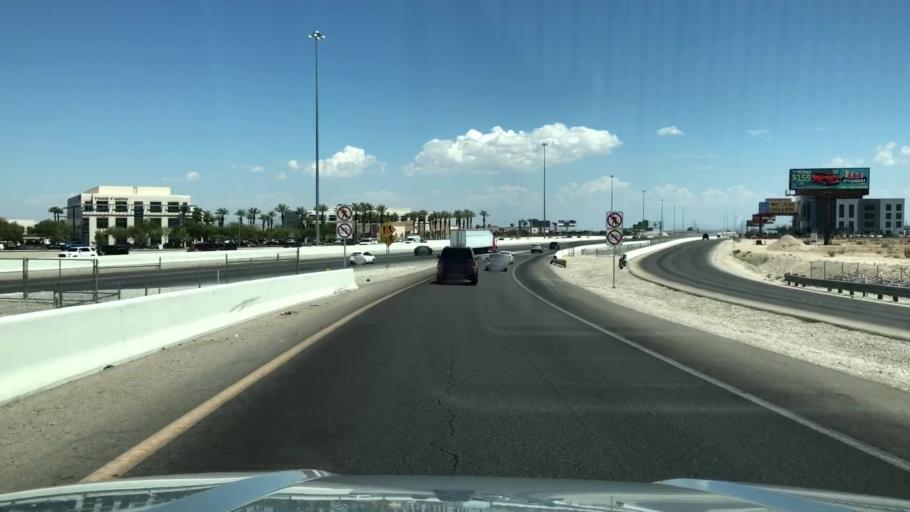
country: US
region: Nevada
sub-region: Clark County
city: Spring Valley
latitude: 36.0657
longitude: -115.2766
